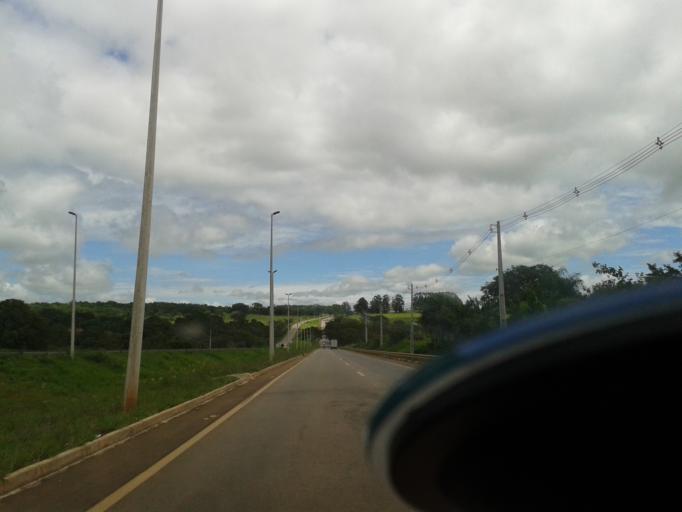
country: BR
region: Goias
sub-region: Inhumas
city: Inhumas
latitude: -16.3538
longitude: -49.5125
